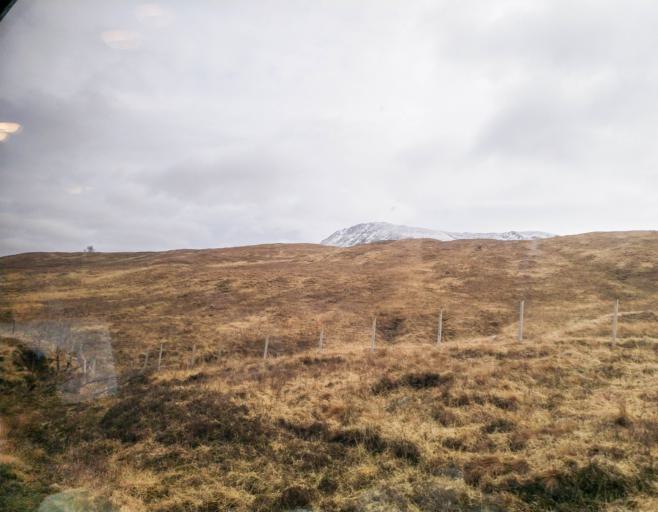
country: GB
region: Scotland
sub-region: Highland
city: Spean Bridge
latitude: 56.5453
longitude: -4.7549
